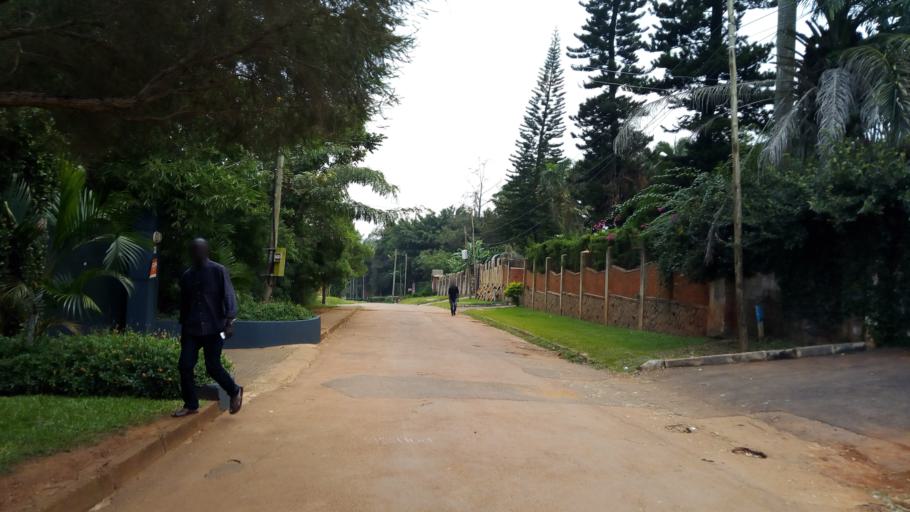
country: UG
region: Central Region
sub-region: Wakiso District
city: Kireka
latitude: 0.3209
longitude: 32.6276
